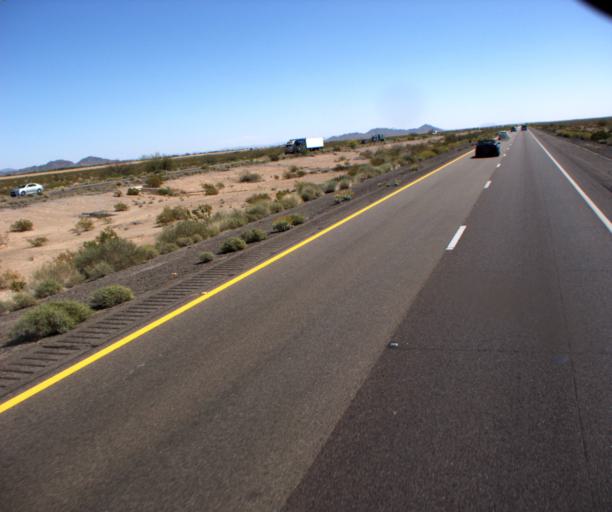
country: US
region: Arizona
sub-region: La Paz County
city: Salome
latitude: 33.6024
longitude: -113.5769
